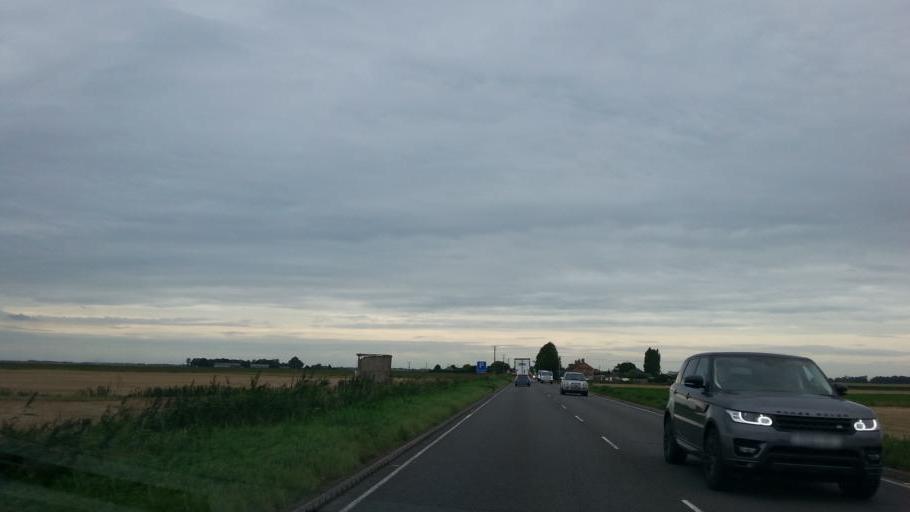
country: GB
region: England
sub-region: Peterborough
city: Thorney
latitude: 52.6155
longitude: -0.0087
